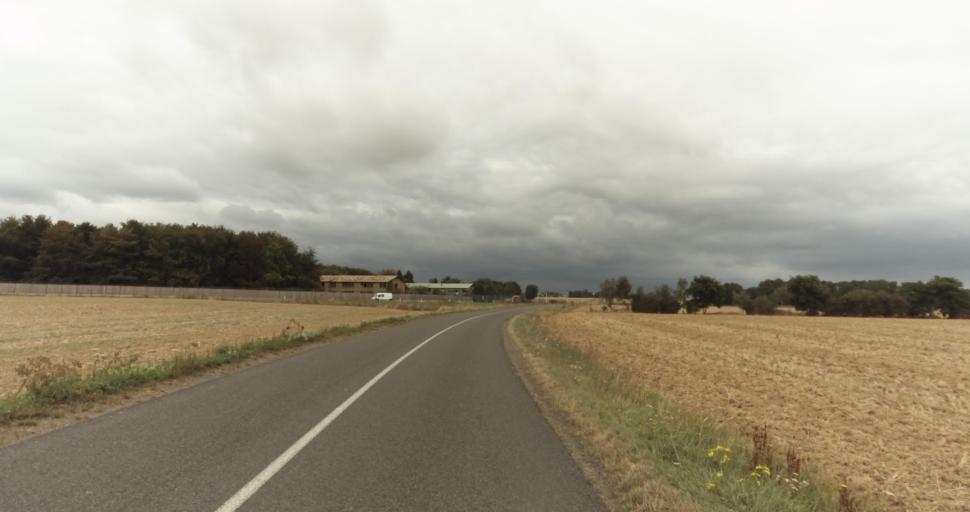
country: FR
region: Haute-Normandie
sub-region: Departement de l'Eure
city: Gravigny
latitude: 49.0440
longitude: 1.2331
